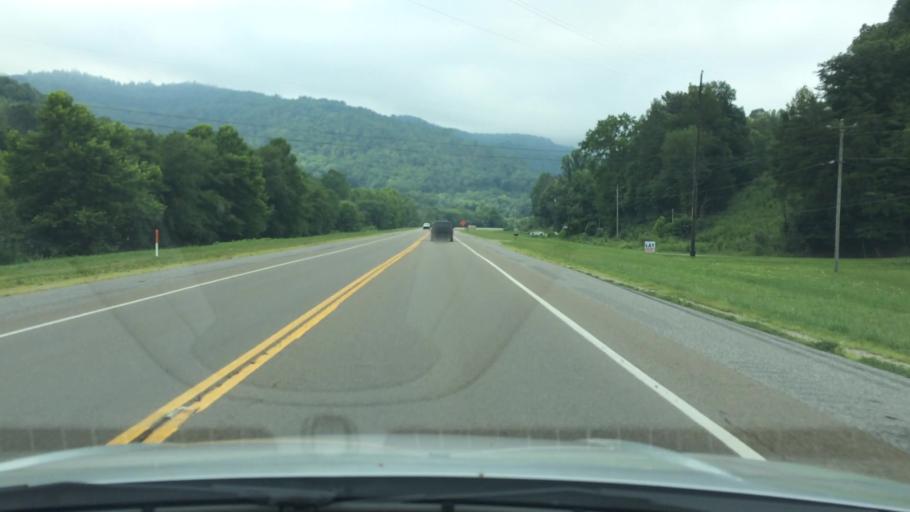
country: US
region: Tennessee
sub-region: Campbell County
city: Caryville
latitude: 36.3894
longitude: -84.3421
